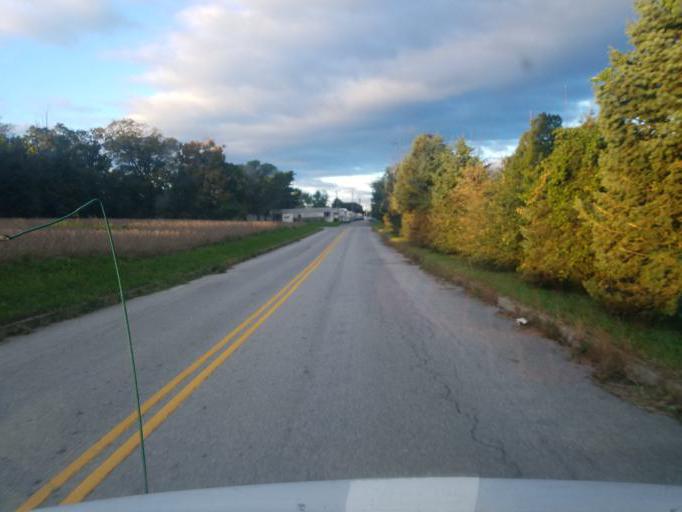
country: US
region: Pennsylvania
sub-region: York County
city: Shiloh
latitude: 39.9340
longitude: -76.8127
